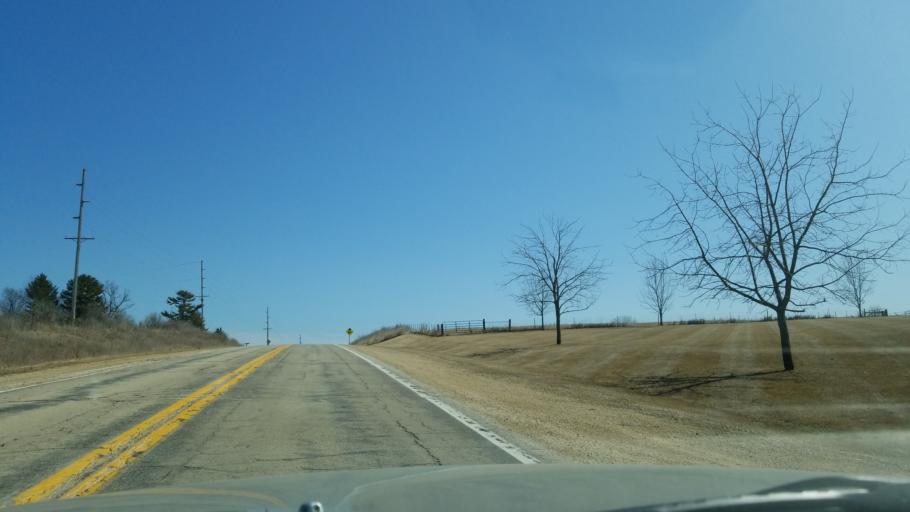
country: US
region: Wisconsin
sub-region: Iowa County
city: Mineral Point
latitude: 42.9126
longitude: -90.2581
